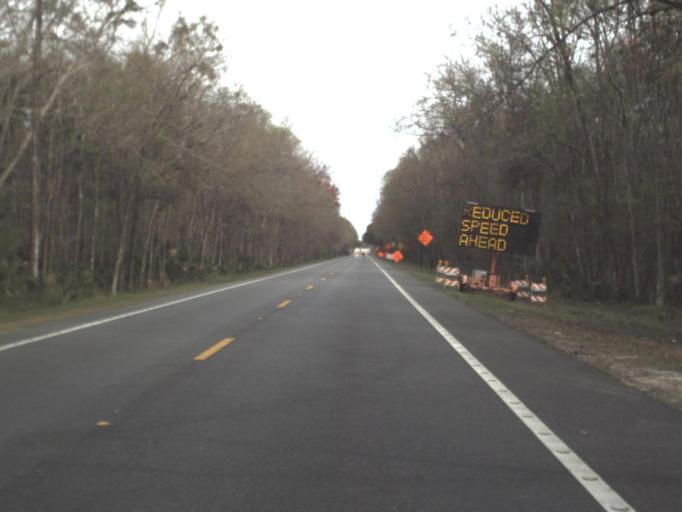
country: US
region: Florida
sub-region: Leon County
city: Woodville
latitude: 30.1510
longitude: -83.9834
